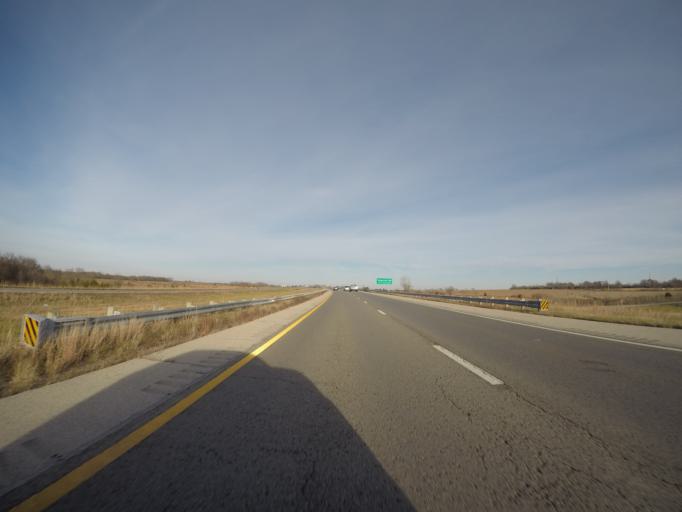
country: US
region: Kansas
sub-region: Douglas County
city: Eudora
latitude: 38.9438
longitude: -95.0394
